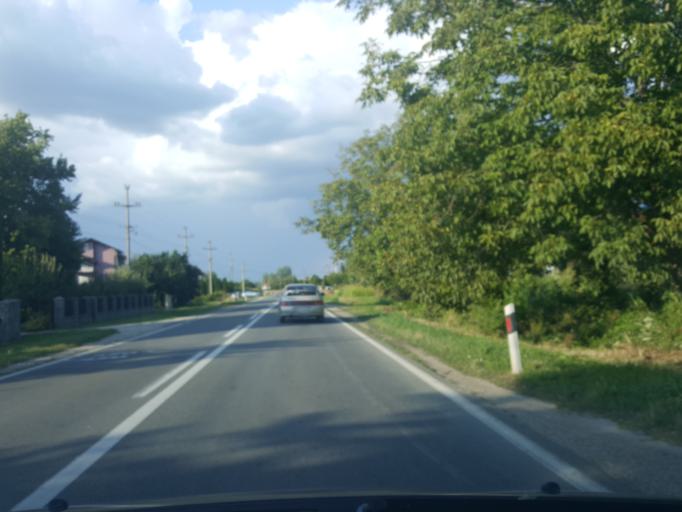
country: RS
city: Lesnica
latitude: 44.6356
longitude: 19.2755
